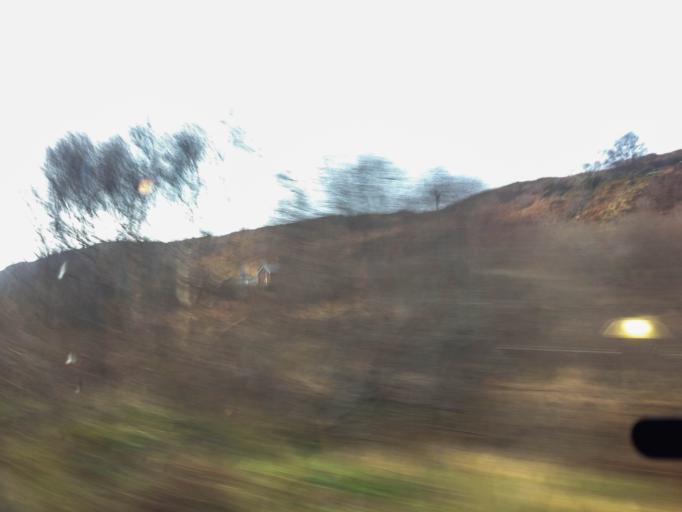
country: GB
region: Scotland
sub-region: Argyll and Bute
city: Isle Of Mull
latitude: 56.9869
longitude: -5.8246
